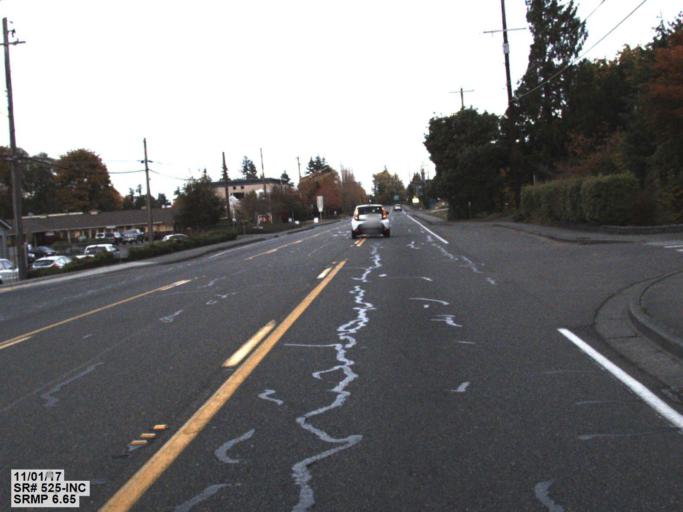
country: US
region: Washington
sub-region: Snohomish County
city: Mukilteo
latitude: 47.9240
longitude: -122.3002
